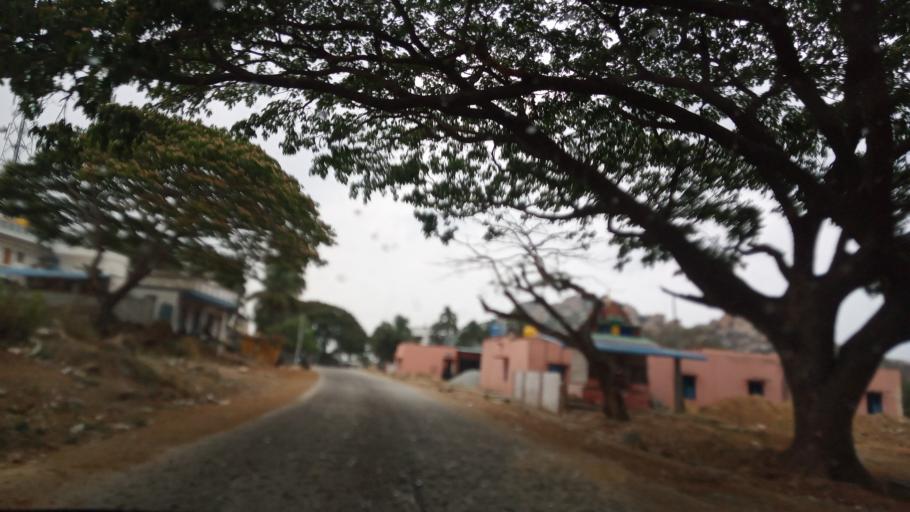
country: IN
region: Karnataka
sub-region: Kolar
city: Mulbagal
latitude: 13.1076
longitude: 78.3328
